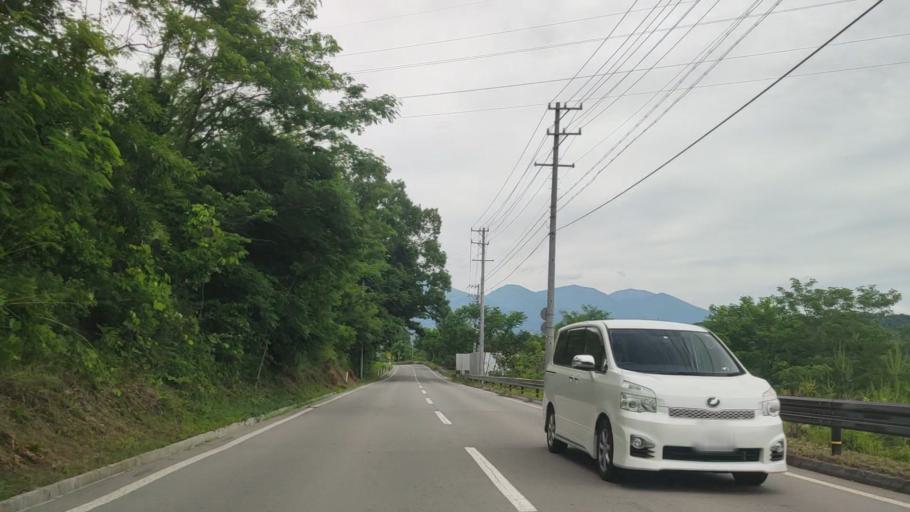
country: JP
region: Nagano
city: Kamimaruko
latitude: 36.3213
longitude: 138.3365
